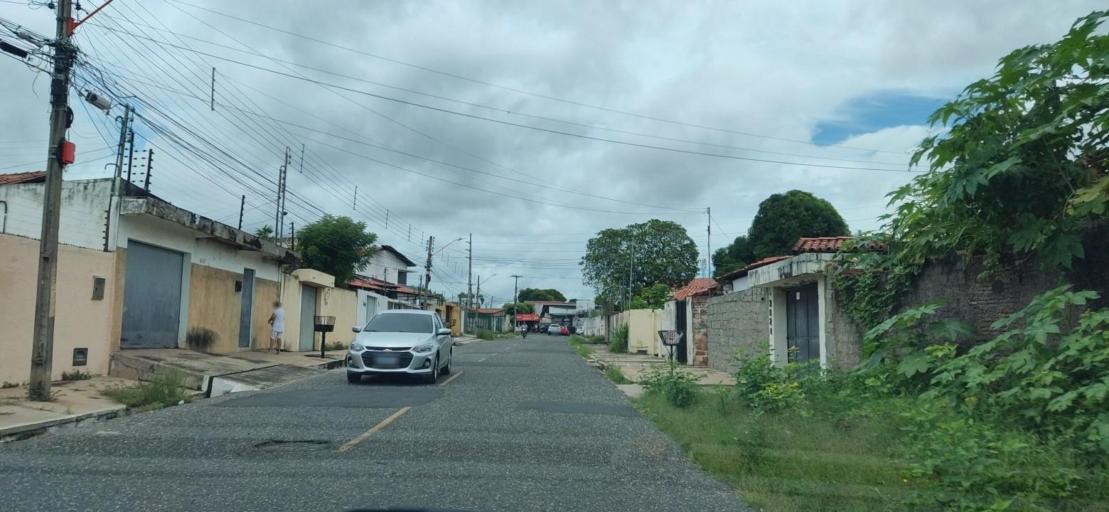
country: BR
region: Piaui
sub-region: Teresina
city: Teresina
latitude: -5.0740
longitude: -42.7652
